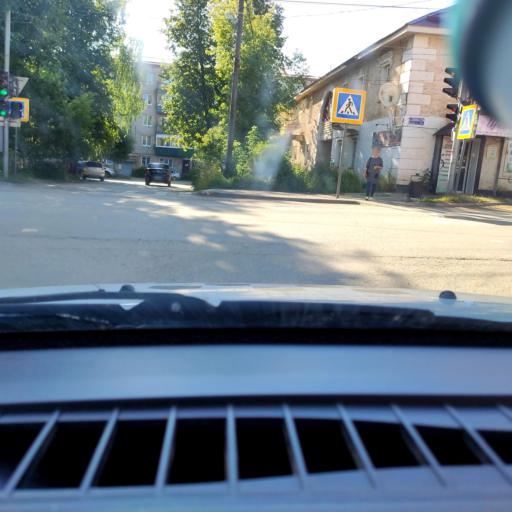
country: RU
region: Perm
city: Ocher
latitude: 57.8836
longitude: 54.7149
